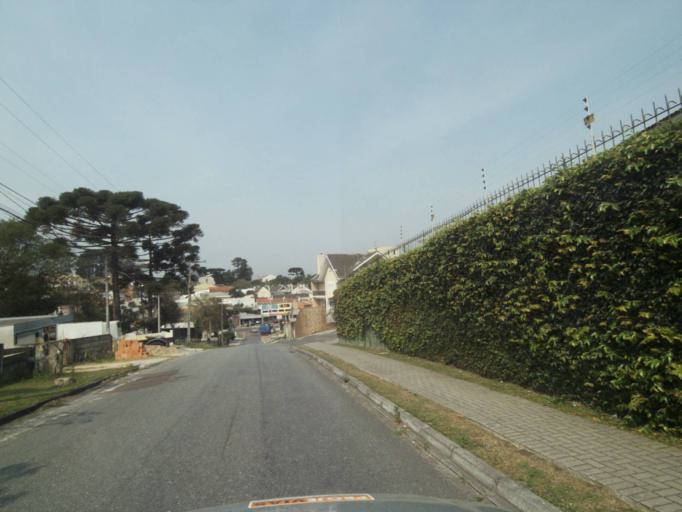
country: BR
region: Parana
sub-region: Pinhais
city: Pinhais
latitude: -25.4817
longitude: -49.2181
